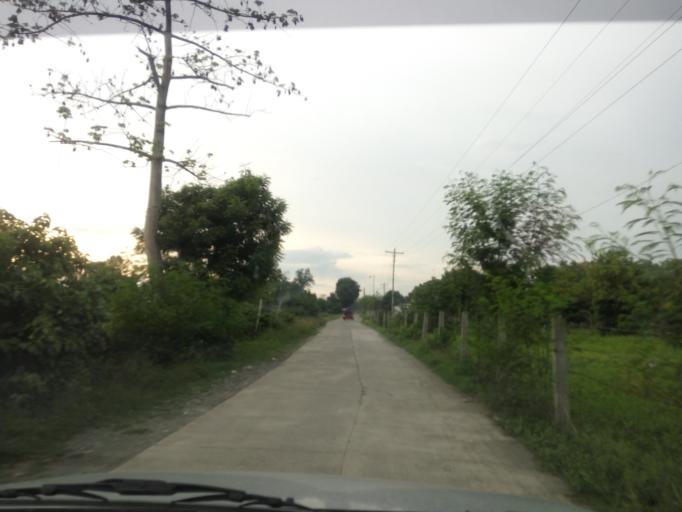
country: PH
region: Ilocos
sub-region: Province of La Union
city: Rosario
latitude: 16.2067
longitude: 120.4712
